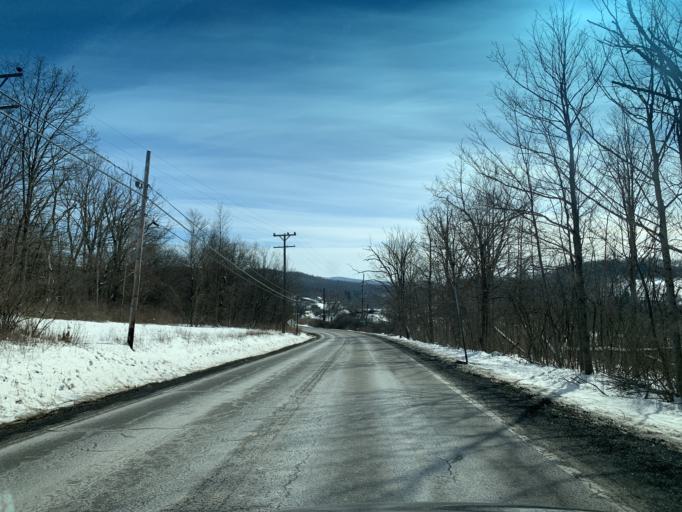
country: US
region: Maryland
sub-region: Allegany County
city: Frostburg
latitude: 39.6218
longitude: -78.9380
